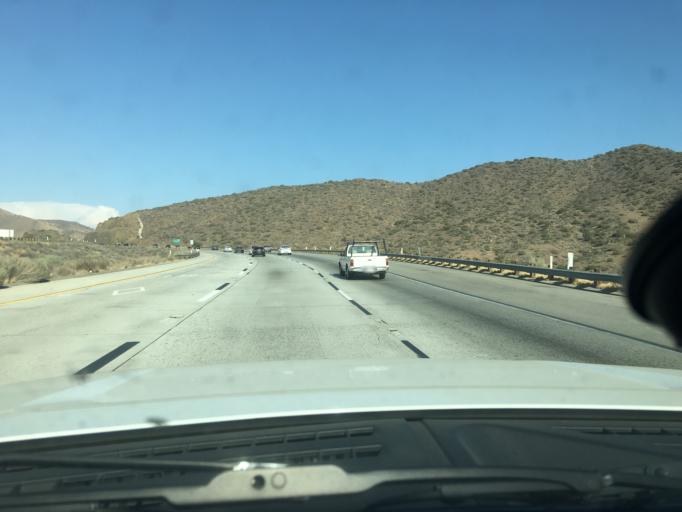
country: US
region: California
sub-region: Los Angeles County
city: Acton
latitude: 34.4922
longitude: -118.1817
